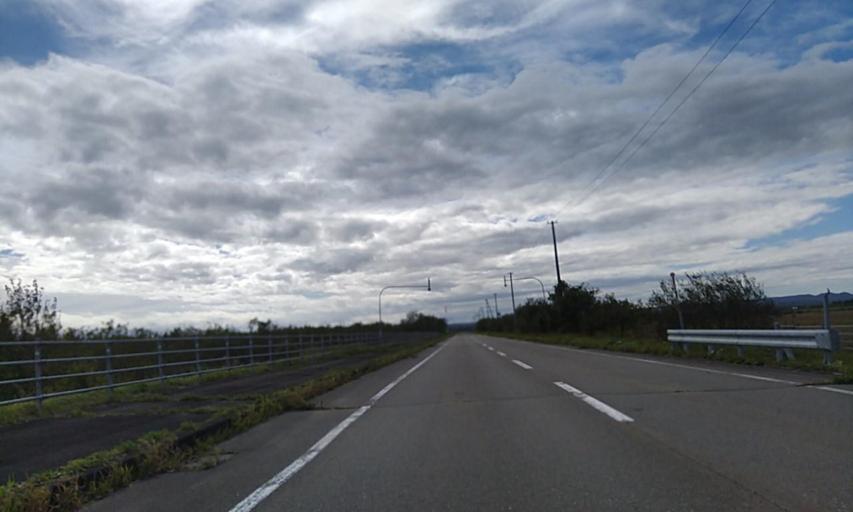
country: JP
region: Hokkaido
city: Obihiro
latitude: 42.7246
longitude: 143.6673
